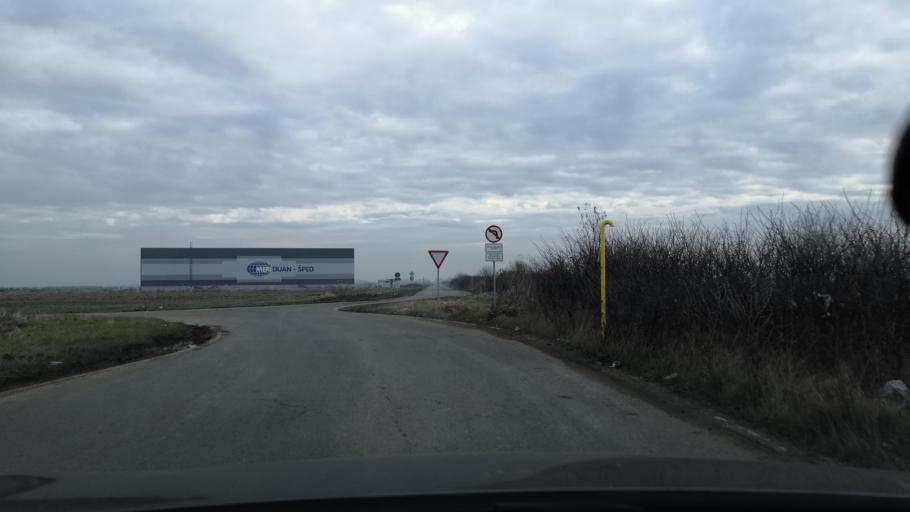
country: RS
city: Ugrinovci
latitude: 44.8822
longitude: 20.1494
